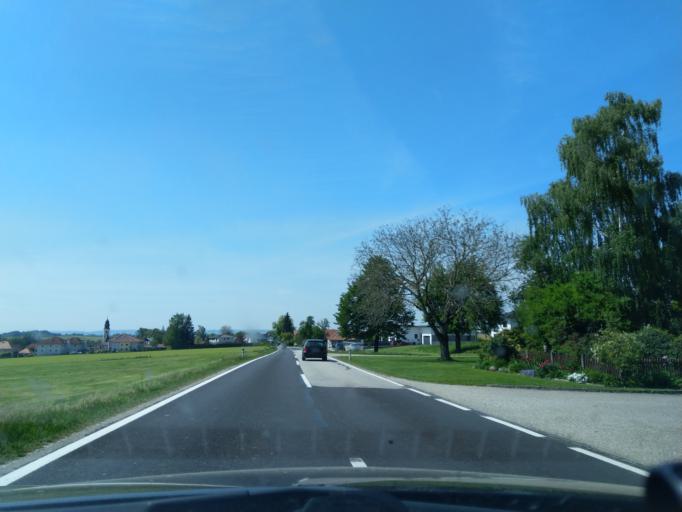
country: DE
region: Bavaria
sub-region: Lower Bavaria
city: Bad Fussing
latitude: 48.2759
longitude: 13.3803
